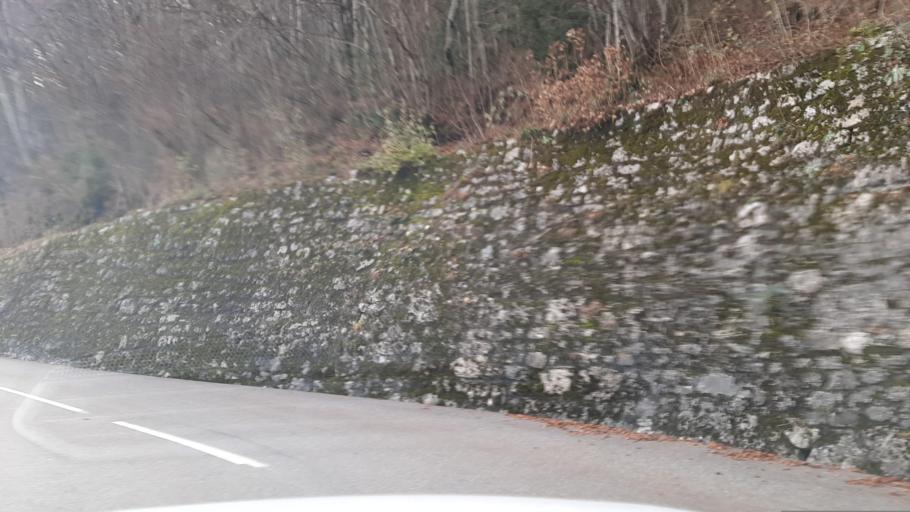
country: FR
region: Rhone-Alpes
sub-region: Departement de la Savoie
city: Coise-Saint-Jean-Pied-Gauthier
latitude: 45.5839
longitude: 6.1443
